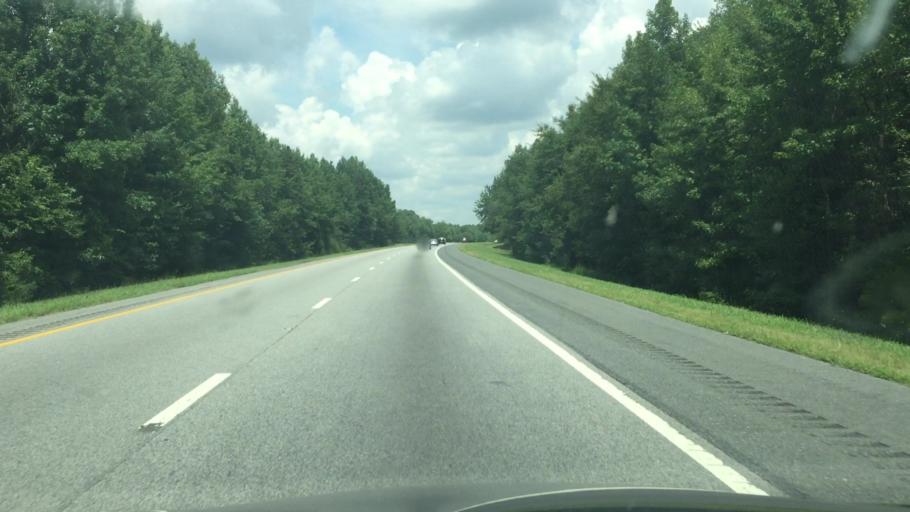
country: US
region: North Carolina
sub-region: Guilford County
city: Pleasant Garden
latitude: 35.9361
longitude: -79.8269
